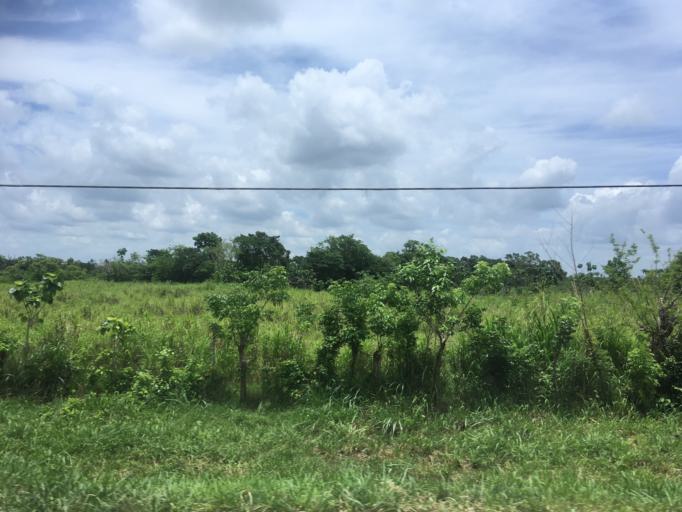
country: CU
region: Villa Clara
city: Esperanza
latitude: 22.4241
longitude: -80.0508
